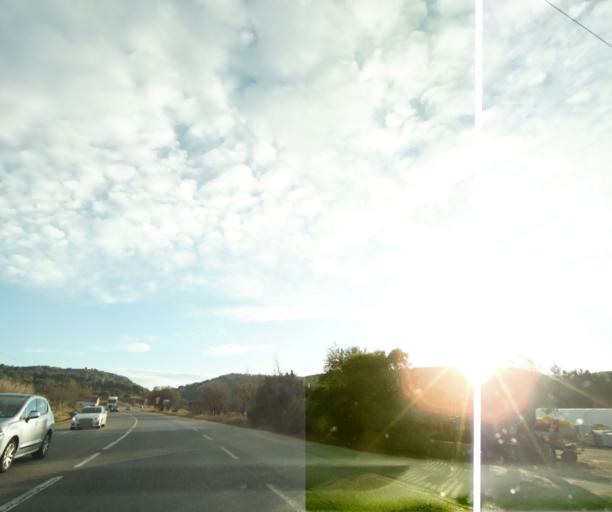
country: FR
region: Provence-Alpes-Cote d'Azur
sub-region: Departement des Bouches-du-Rhone
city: Chateauneuf-les-Martigues
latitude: 43.3771
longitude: 5.1866
